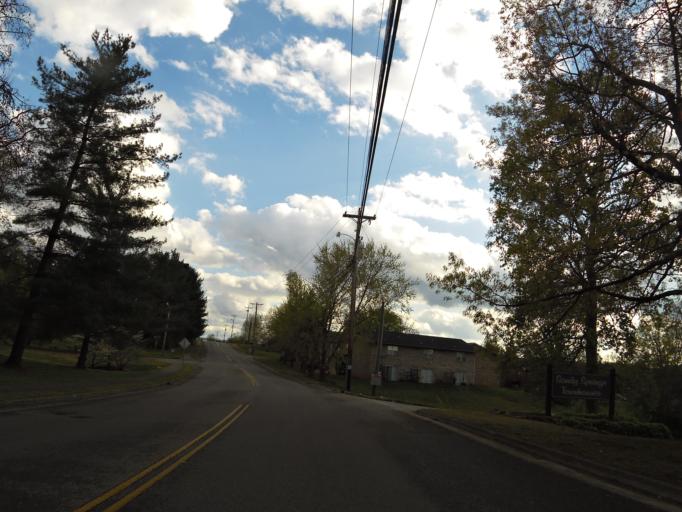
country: US
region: Tennessee
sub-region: Blount County
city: Maryville
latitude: 35.7330
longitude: -83.9788
